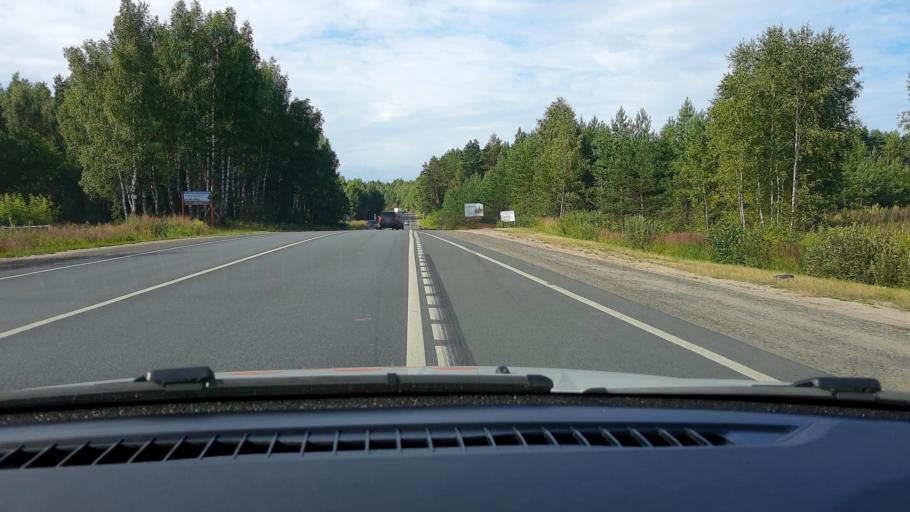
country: RU
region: Nizjnij Novgorod
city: Arzamas
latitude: 55.5146
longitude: 43.9022
